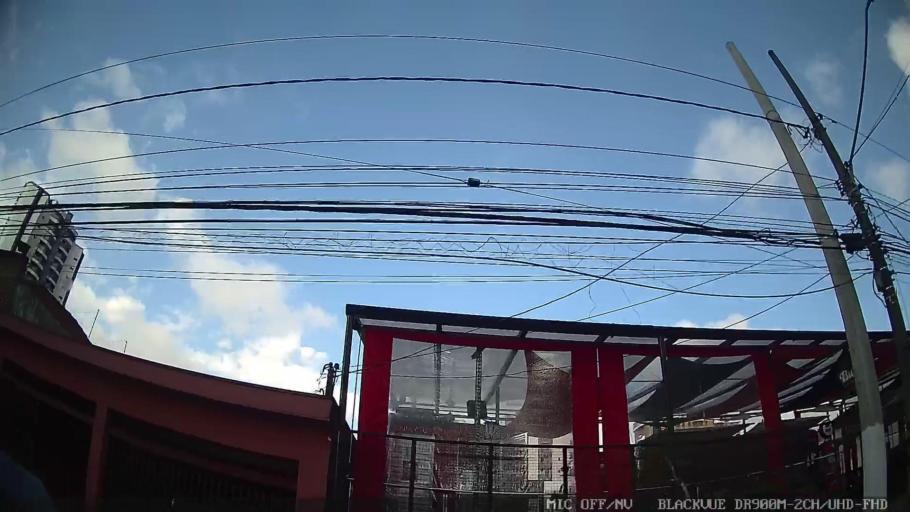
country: BR
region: Sao Paulo
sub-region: Sao Caetano Do Sul
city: Sao Caetano do Sul
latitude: -23.5479
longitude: -46.5577
